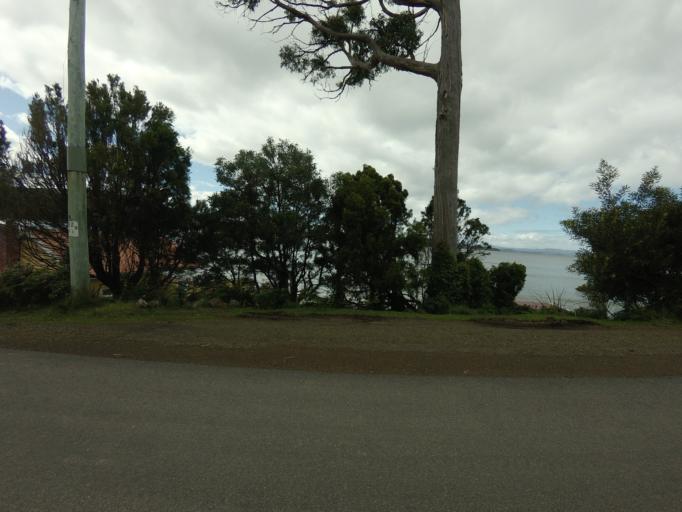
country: AU
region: Tasmania
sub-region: Huon Valley
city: Geeveston
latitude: -43.4433
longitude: 146.9610
